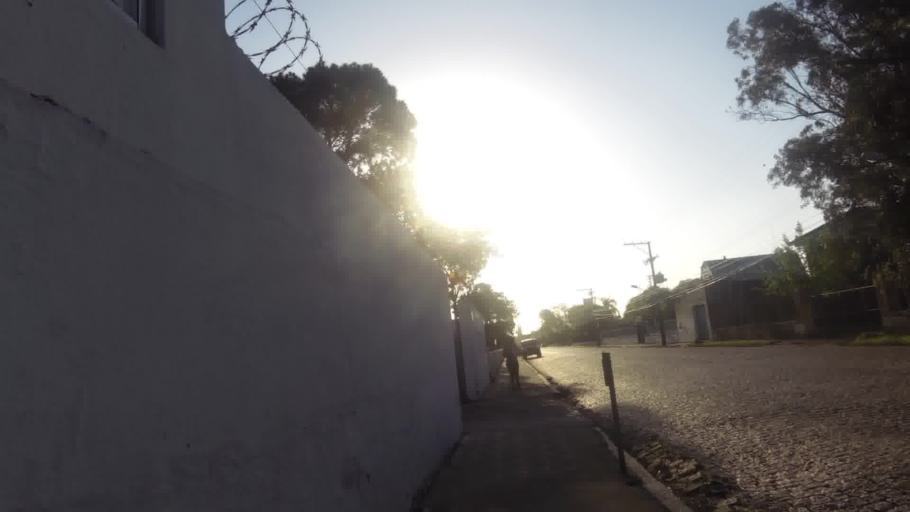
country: BR
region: Rio Grande do Sul
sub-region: Rio Grande
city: Rio Grande
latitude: -32.0311
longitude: -52.0810
